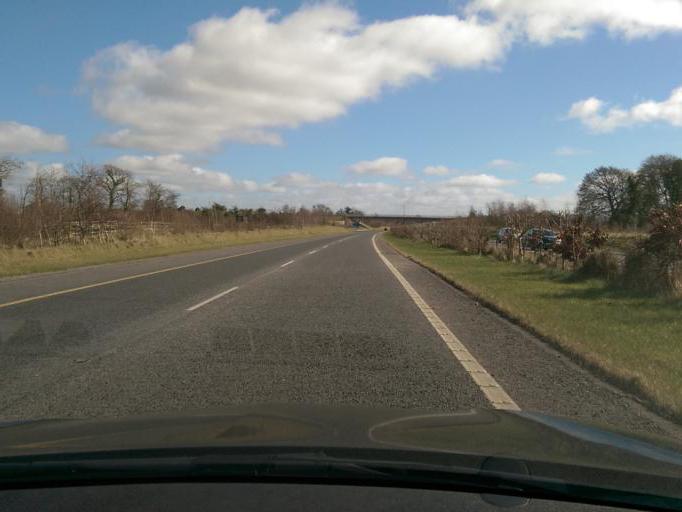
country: IE
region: Leinster
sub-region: An Mhi
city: Longwood
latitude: 53.4259
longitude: -6.9655
